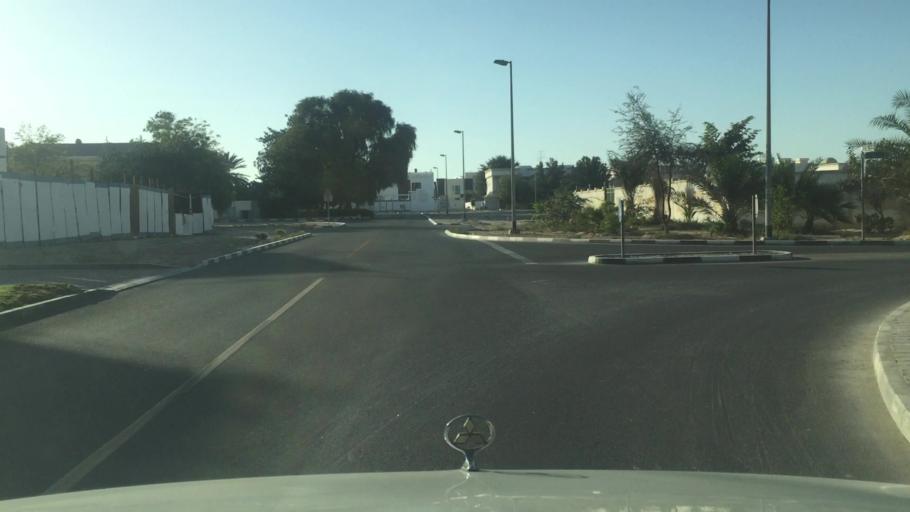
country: AE
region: Dubai
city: Dubai
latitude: 25.1622
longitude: 55.2282
